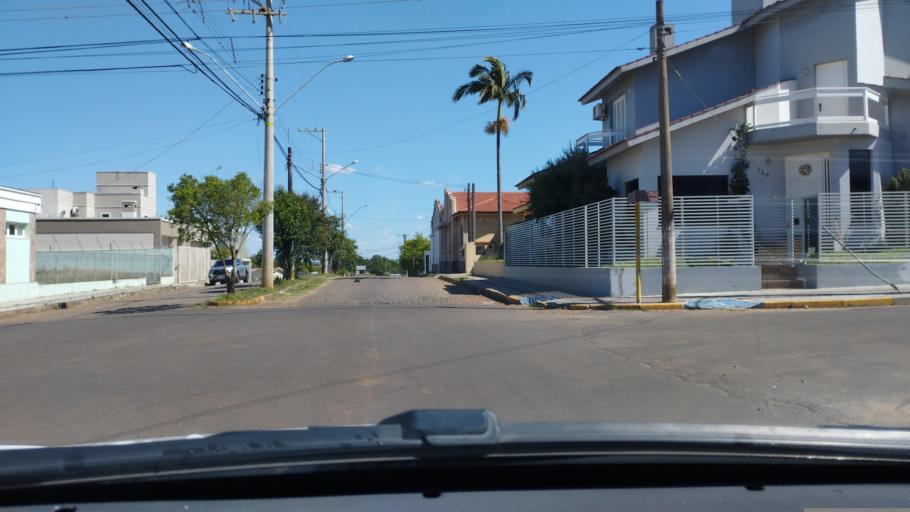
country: BR
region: Rio Grande do Sul
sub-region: Tupancireta
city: Tupancireta
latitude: -29.0868
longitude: -53.8352
